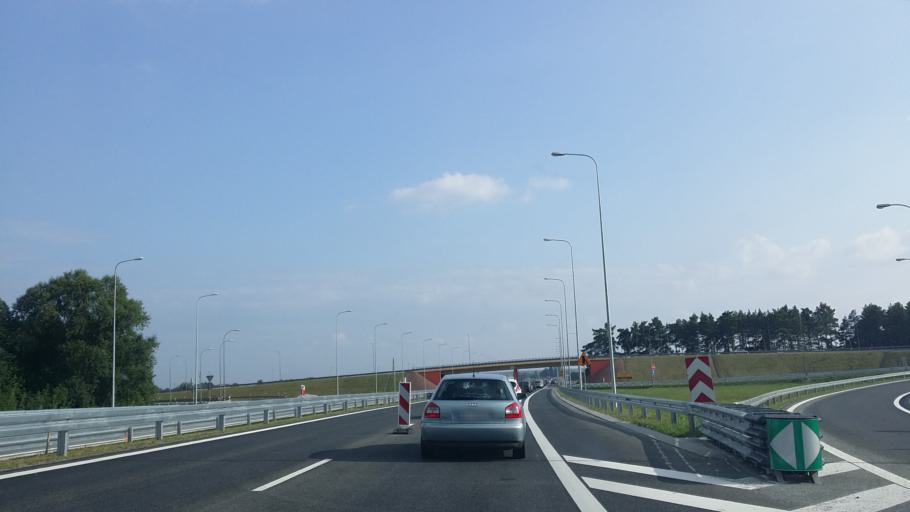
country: PL
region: Lubusz
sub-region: Powiat miedzyrzecki
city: Miedzyrzecz
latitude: 52.4651
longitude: 15.5646
